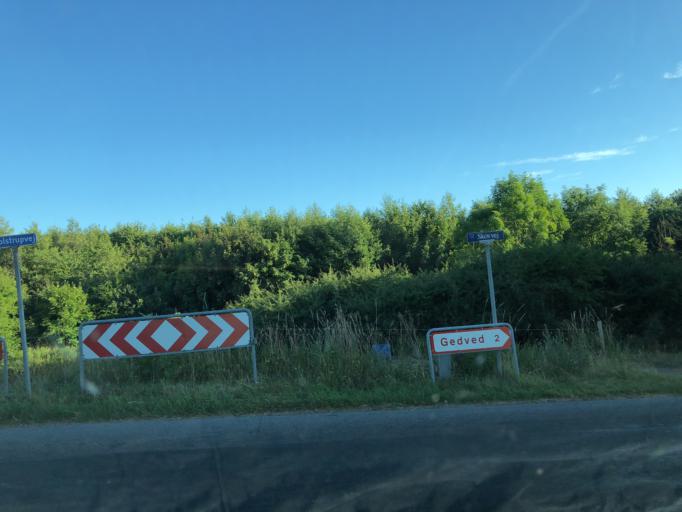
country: DK
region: Central Jutland
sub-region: Horsens Kommune
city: Horsens
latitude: 55.9243
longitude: 9.8649
